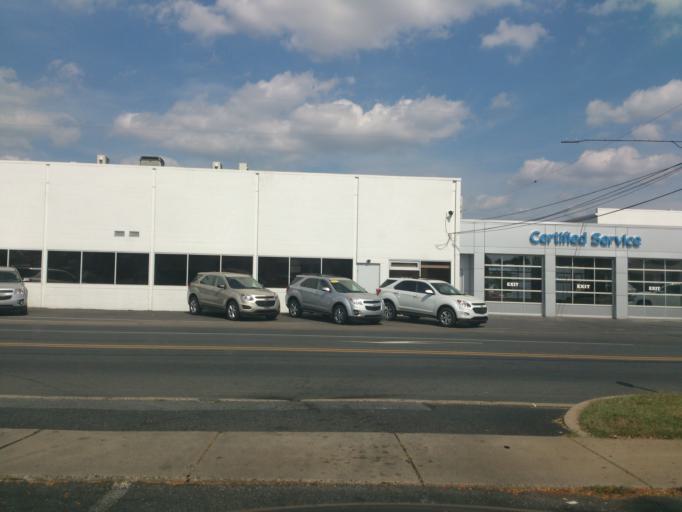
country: US
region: Pennsylvania
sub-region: Lebanon County
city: Palmyra
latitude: 40.3113
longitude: -76.5869
